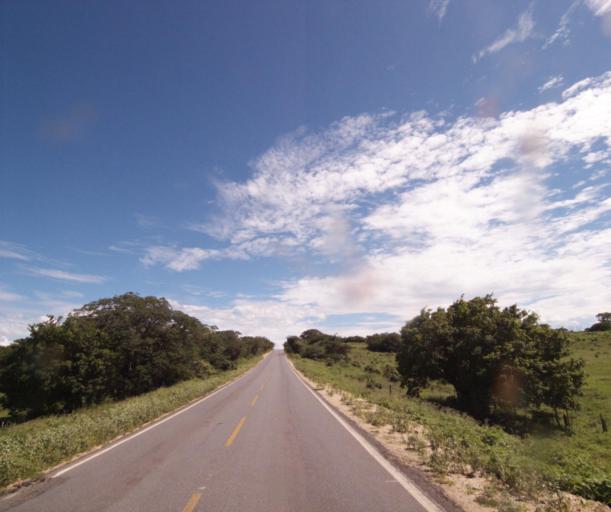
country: BR
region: Bahia
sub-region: Guanambi
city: Guanambi
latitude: -14.5663
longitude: -42.7027
